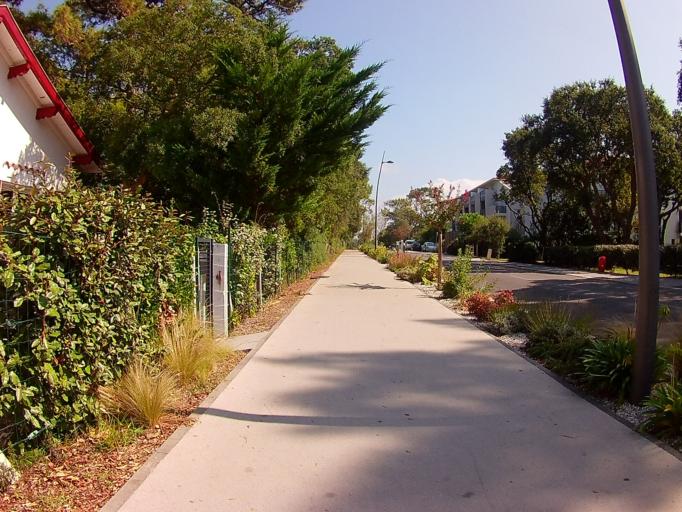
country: FR
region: Aquitaine
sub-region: Departement des Landes
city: Ondres
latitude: 43.5977
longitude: -1.4678
